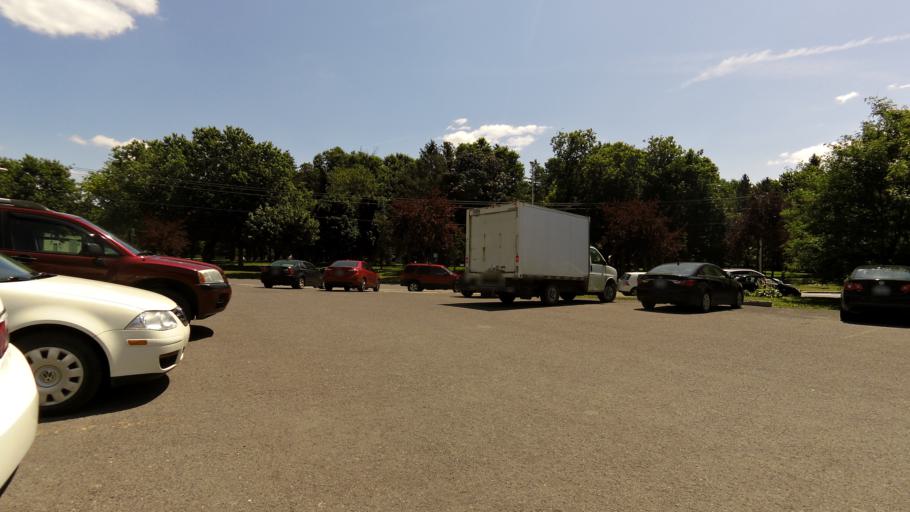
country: CA
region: Quebec
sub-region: Monteregie
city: Saint-Jean-sur-Richelieu
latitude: 45.3195
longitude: -73.2637
